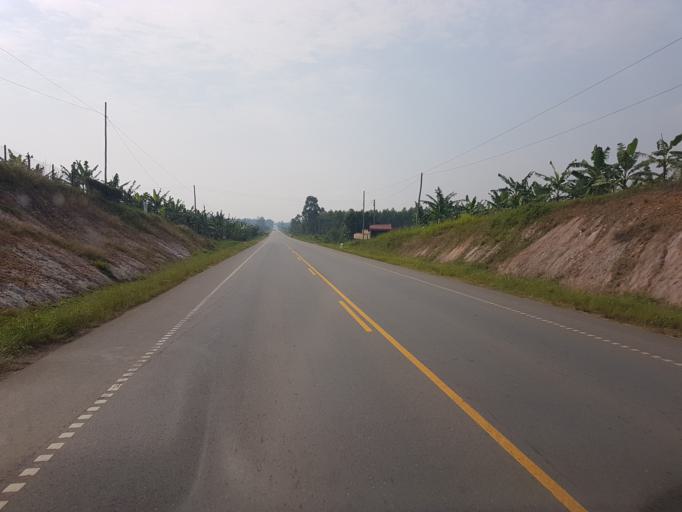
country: UG
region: Western Region
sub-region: Mbarara District
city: Bwizibwera
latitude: -0.6354
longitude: 30.5392
